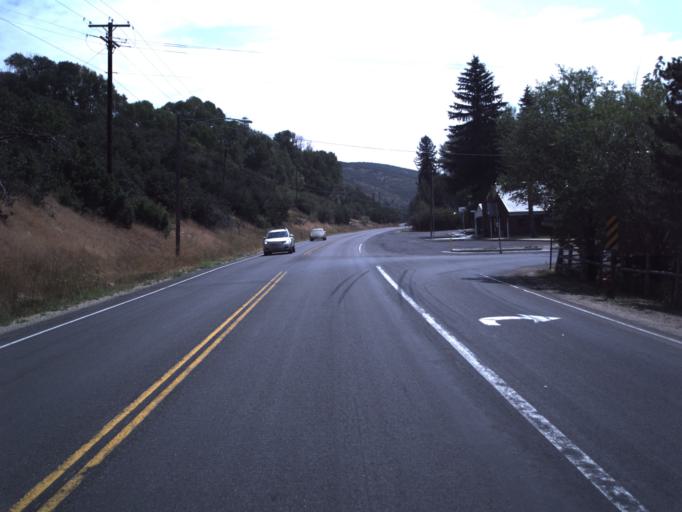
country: US
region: Utah
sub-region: Summit County
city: Francis
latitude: 40.5815
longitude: -111.2278
